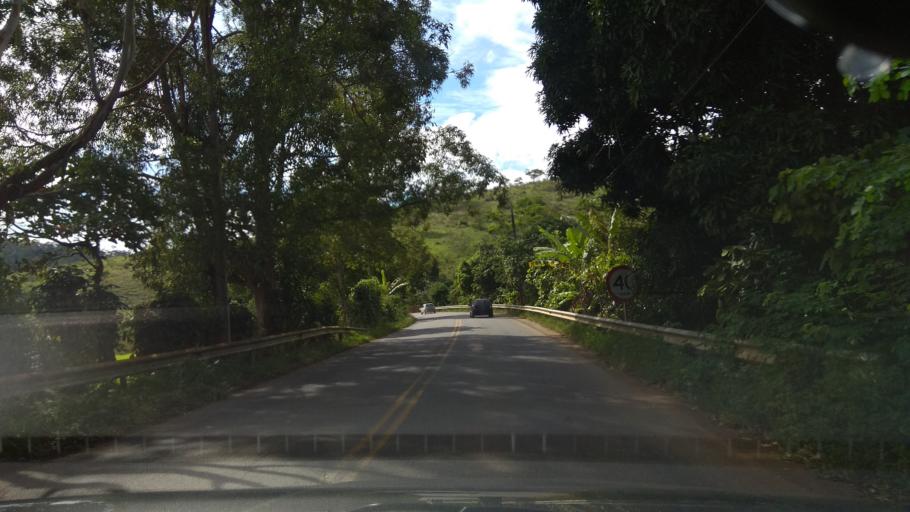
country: BR
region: Bahia
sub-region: Ubaira
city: Ubaira
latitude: -13.2716
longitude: -39.6321
